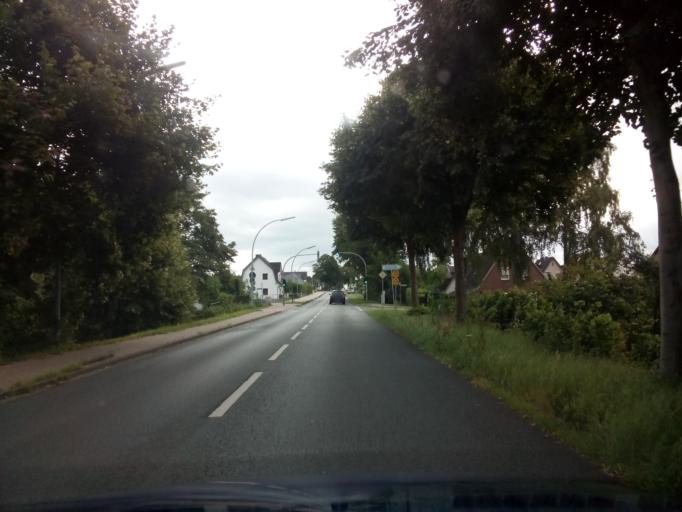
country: DE
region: Lower Saxony
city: Osterholz-Scharmbeck
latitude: 53.2168
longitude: 8.7842
